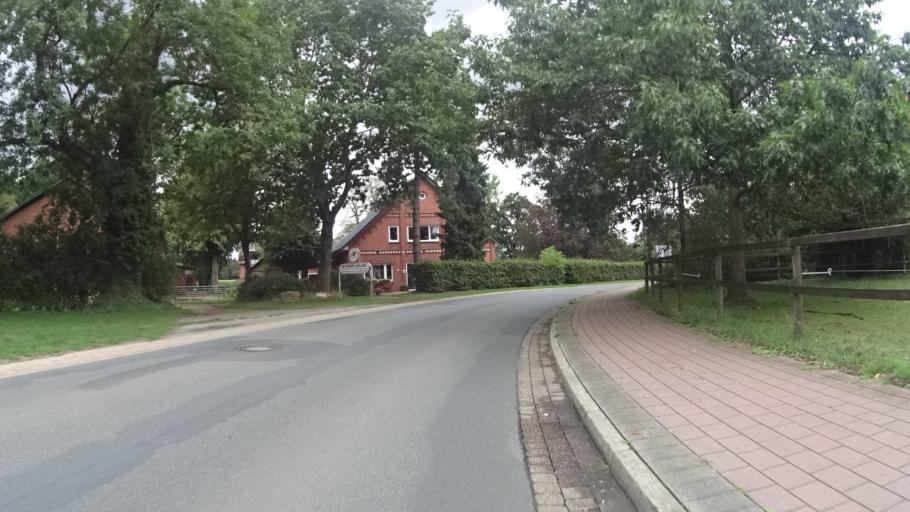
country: DE
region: Lower Saxony
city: Kuhrstedt
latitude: 53.5822
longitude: 8.7999
